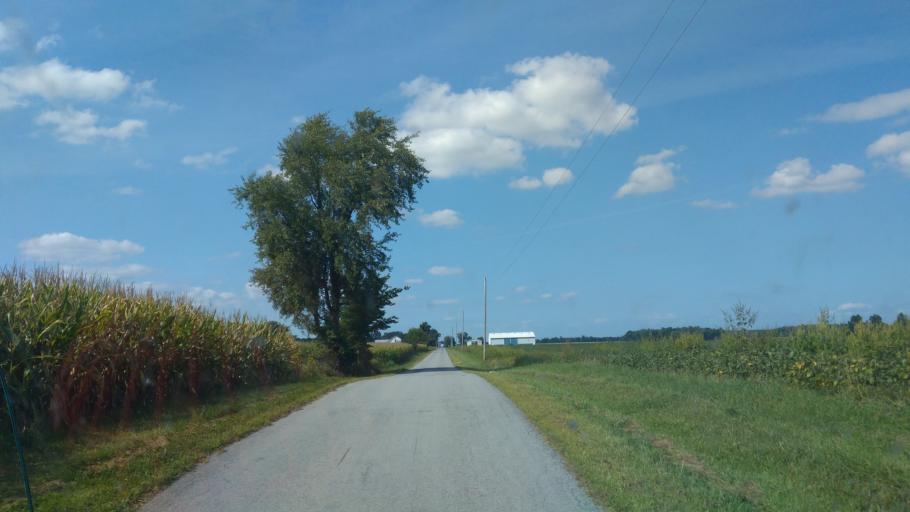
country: US
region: Ohio
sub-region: Hardin County
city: Forest
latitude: 40.7169
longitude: -83.4779
